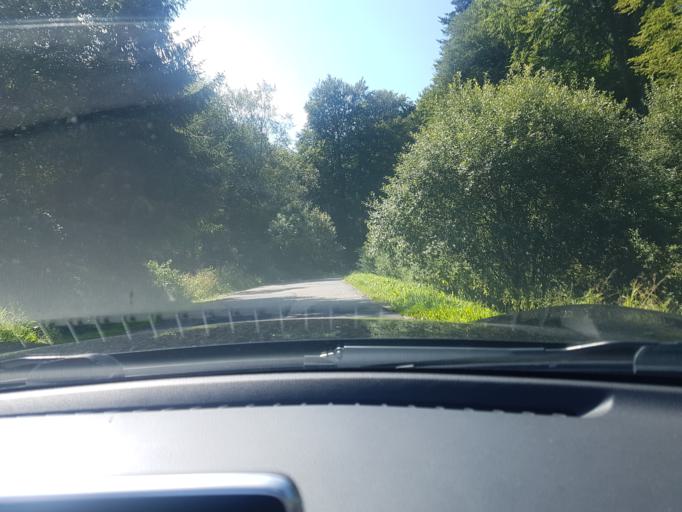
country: DE
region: Baden-Wuerttemberg
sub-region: Karlsruhe Region
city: Limbach
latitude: 49.4954
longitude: 9.2577
